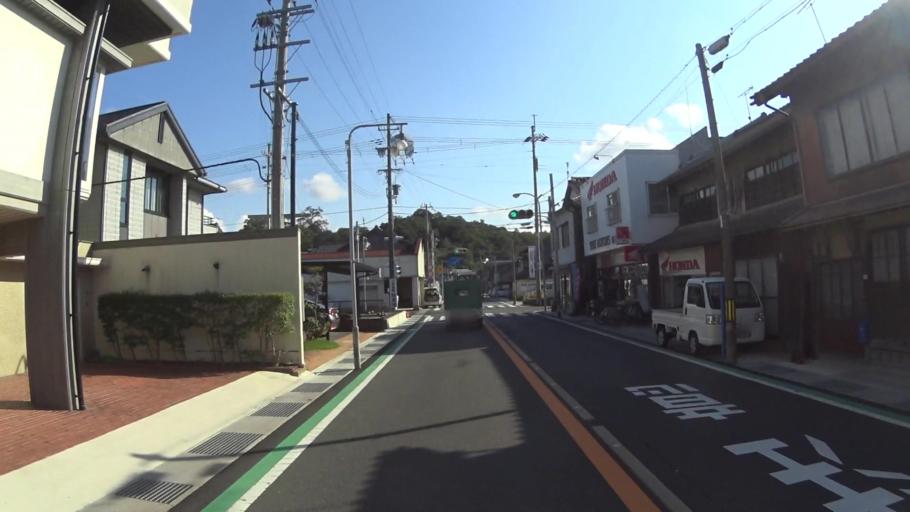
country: JP
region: Kyoto
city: Miyazu
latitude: 35.6815
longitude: 135.0304
